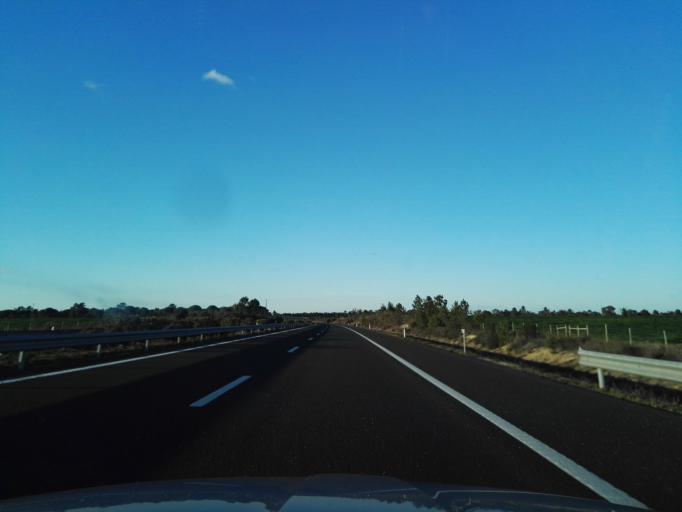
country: PT
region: Santarem
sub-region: Benavente
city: Poceirao
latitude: 38.7795
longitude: -8.6843
